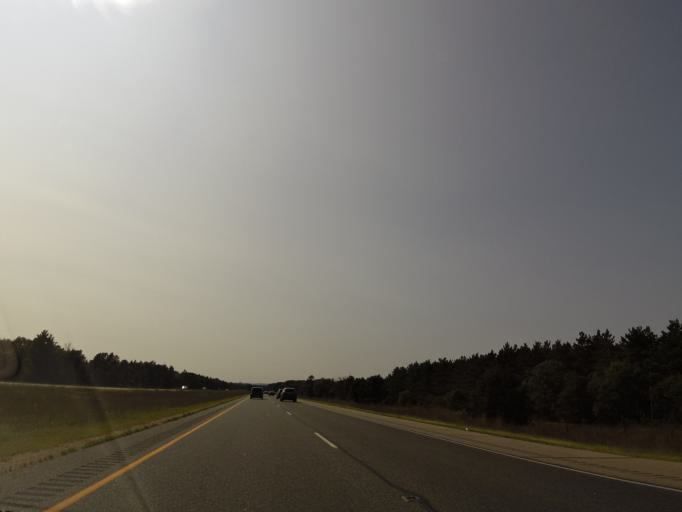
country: US
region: Wisconsin
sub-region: Monroe County
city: Tomah
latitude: 43.9397
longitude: -90.6377
